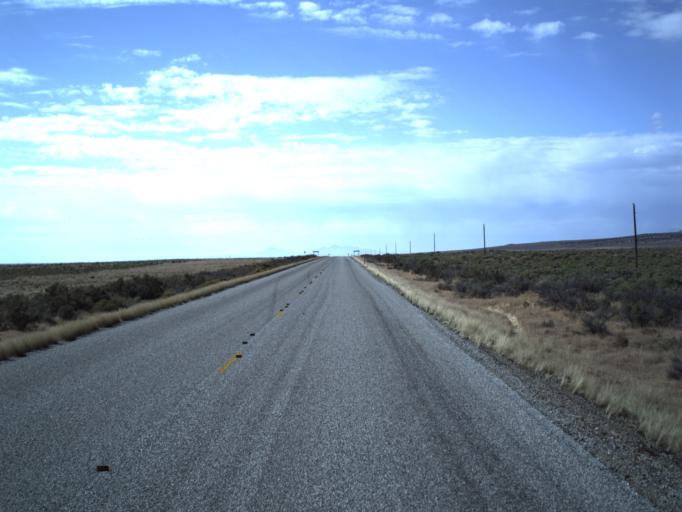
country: US
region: Utah
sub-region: Tooele County
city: Wendover
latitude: 41.5564
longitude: -113.5848
